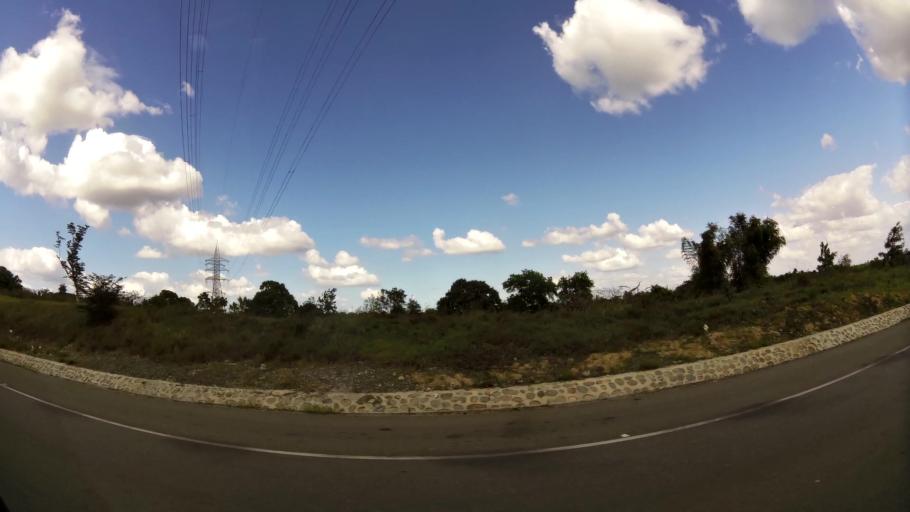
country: DO
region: Santo Domingo
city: Santo Domingo Oeste
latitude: 18.5388
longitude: -70.0770
